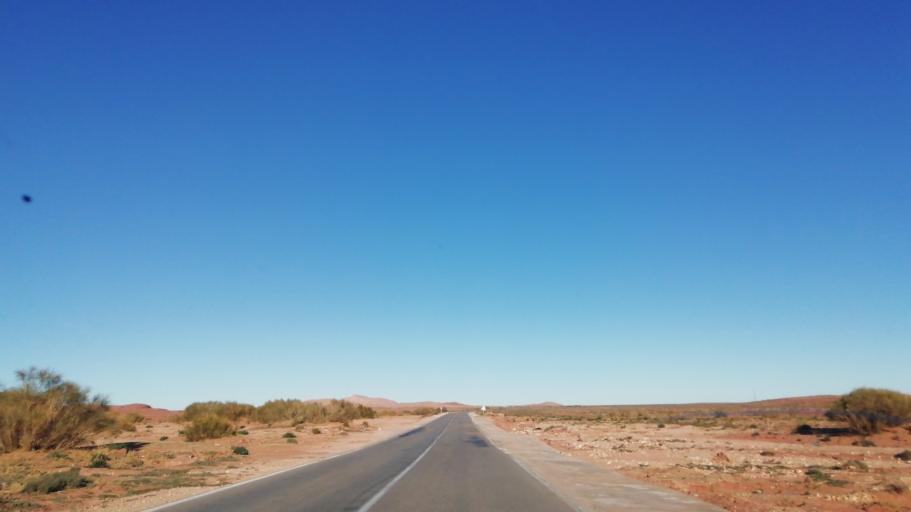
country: DZ
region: El Bayadh
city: El Abiodh Sidi Cheikh
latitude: 33.1076
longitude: 0.2189
